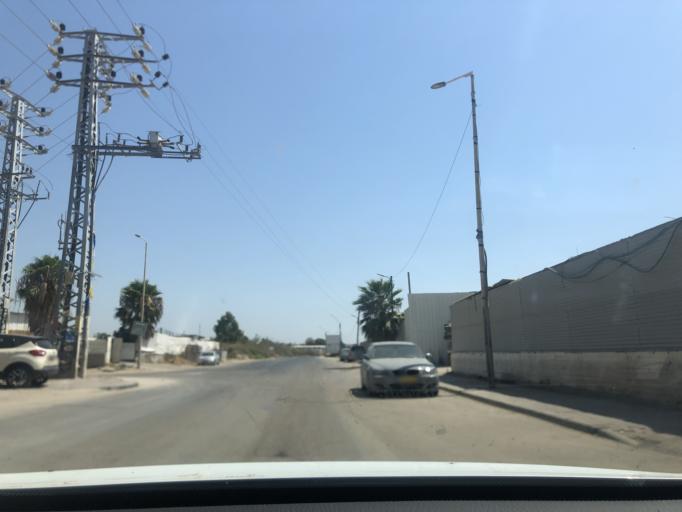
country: IL
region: Central District
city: Lod
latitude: 31.9660
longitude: 34.8921
